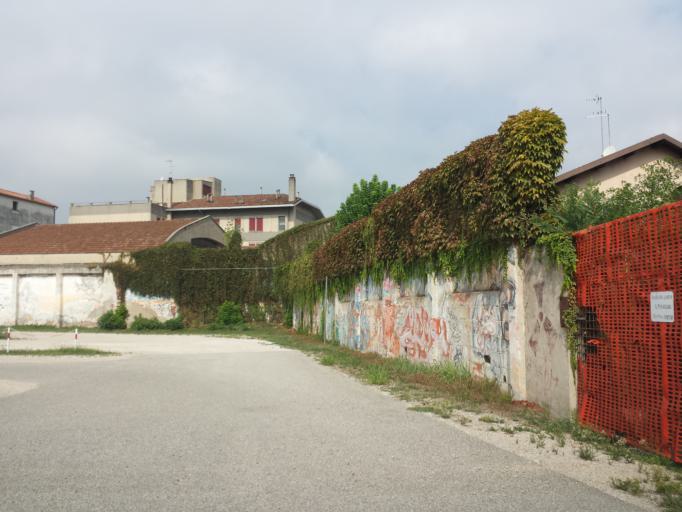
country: IT
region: Veneto
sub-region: Provincia di Padova
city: Padova
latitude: 45.4182
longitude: 11.8757
